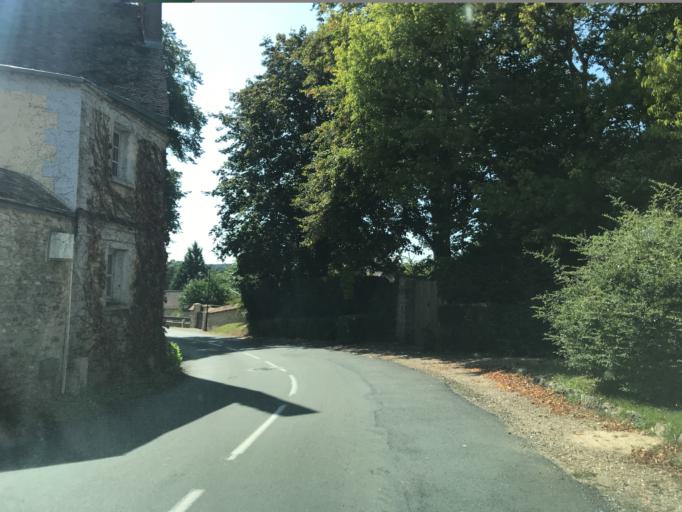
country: FR
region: Haute-Normandie
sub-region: Departement de l'Eure
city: La Chapelle-Reanville
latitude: 49.0970
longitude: 1.3789
